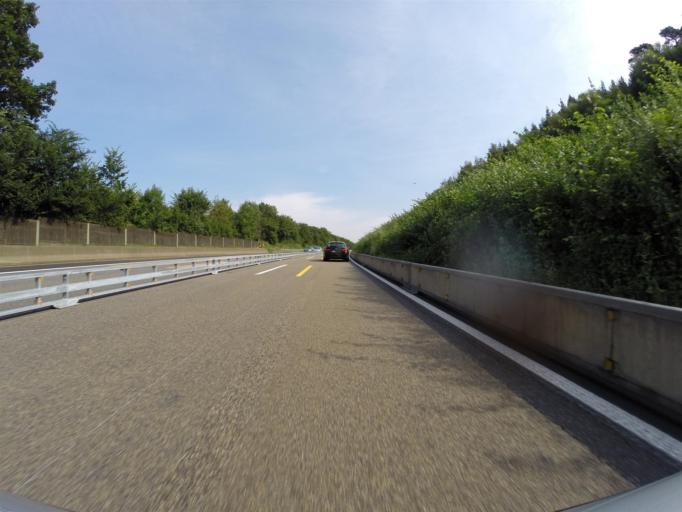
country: DE
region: Hesse
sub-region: Regierungsbezirk Kassel
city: Homberg
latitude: 50.9988
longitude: 9.4752
